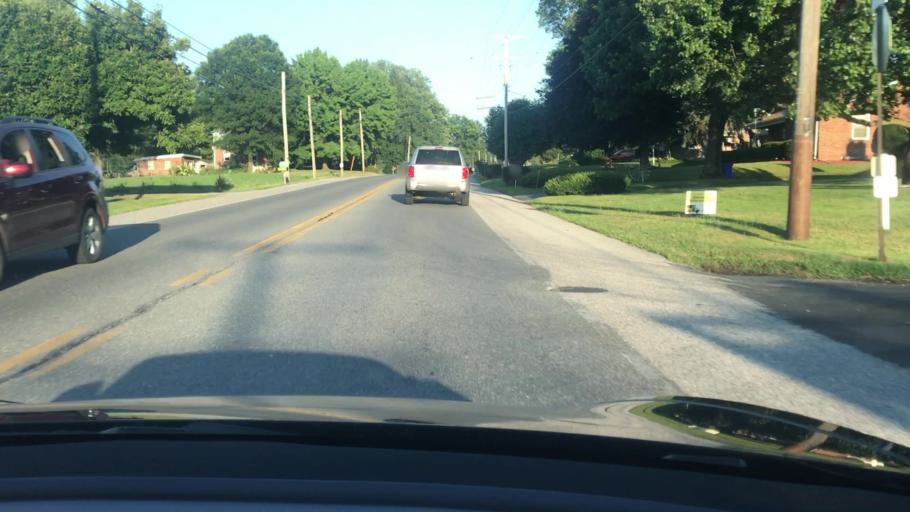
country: US
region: Pennsylvania
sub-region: York County
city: Weigelstown
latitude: 39.9880
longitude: -76.8341
